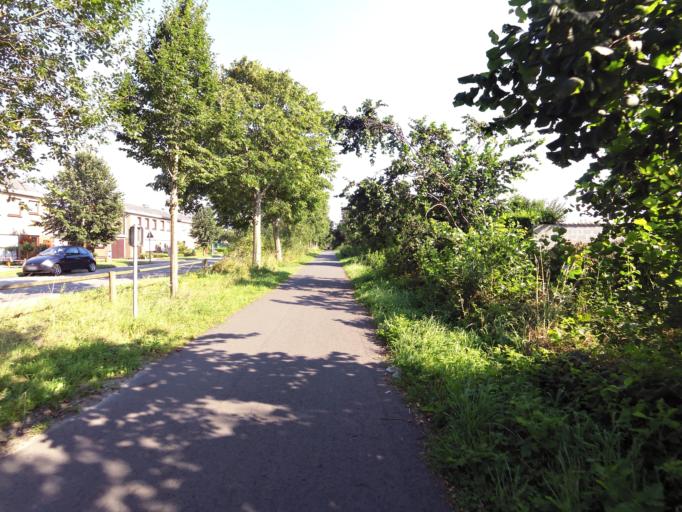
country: BE
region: Flanders
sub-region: Provincie West-Vlaanderen
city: Gistel
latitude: 51.1585
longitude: 2.9571
